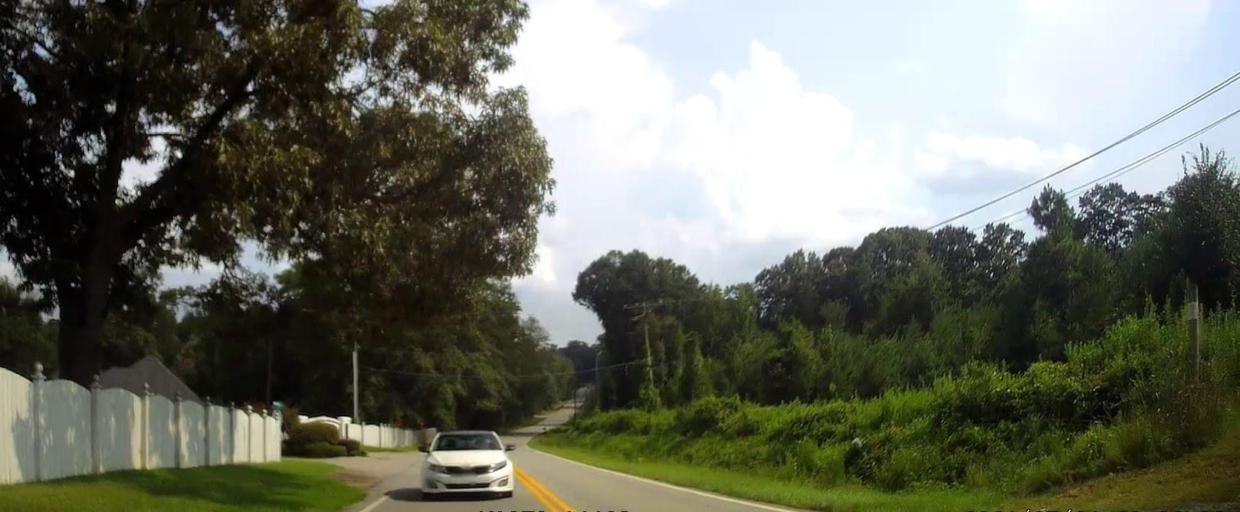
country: US
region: Georgia
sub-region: Houston County
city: Robins Air Force Base
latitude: 32.5746
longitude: -83.6100
